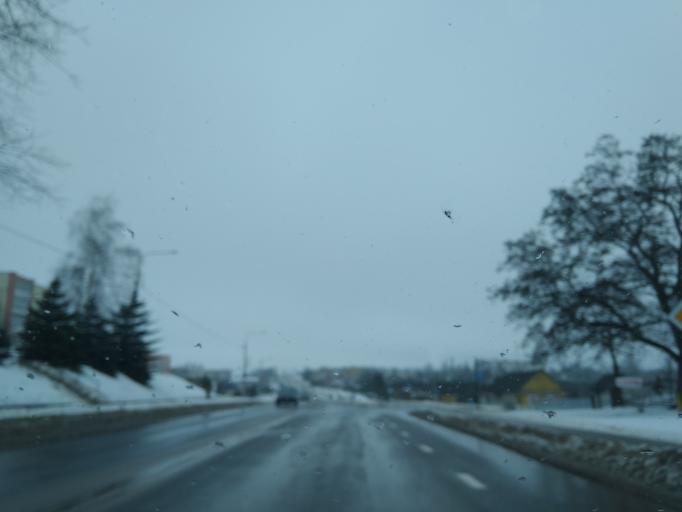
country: BY
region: Minsk
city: Nyasvizh
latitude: 53.2324
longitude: 26.6534
